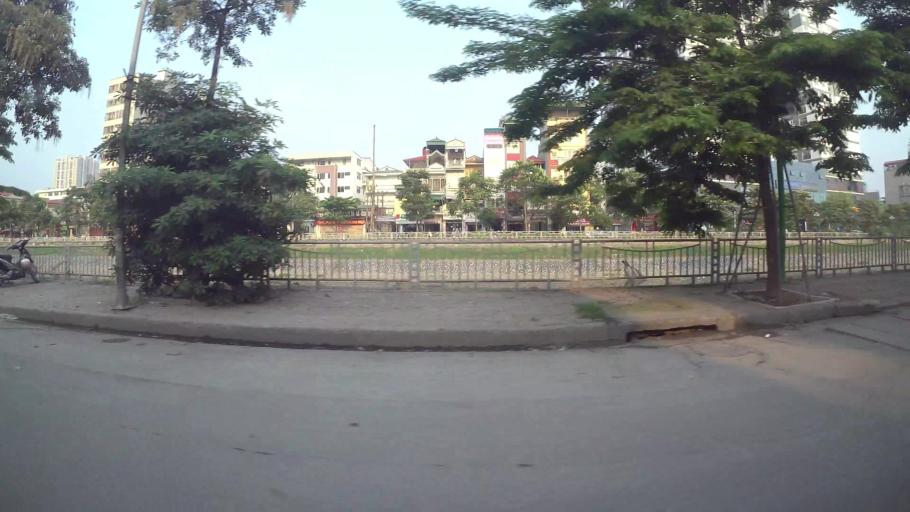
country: VN
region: Ha Noi
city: Thanh Xuan
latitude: 20.9918
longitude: 105.8134
